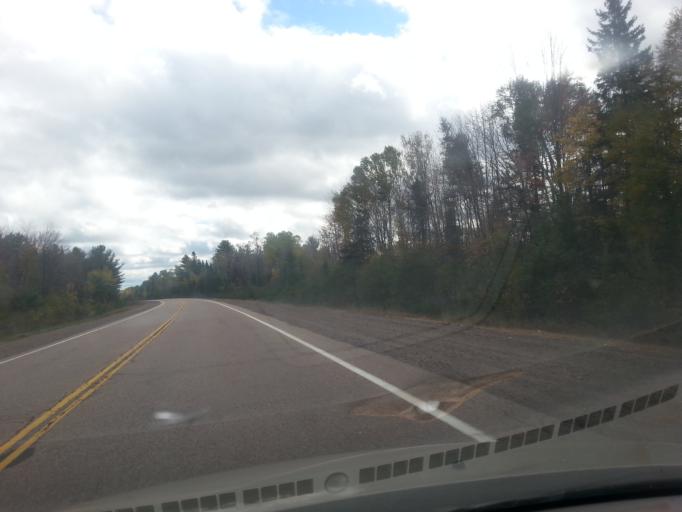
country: CA
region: Ontario
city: Petawawa
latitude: 45.8468
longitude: -77.2740
